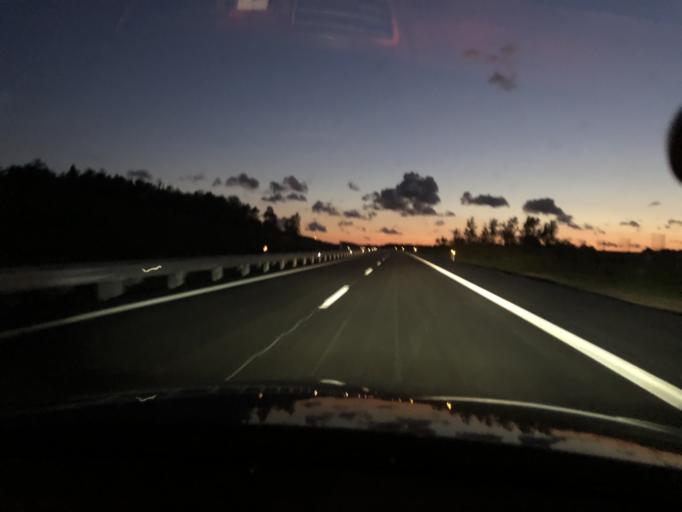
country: DK
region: Zealand
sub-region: Soro Kommune
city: Stenlille
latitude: 55.6607
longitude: 11.5834
